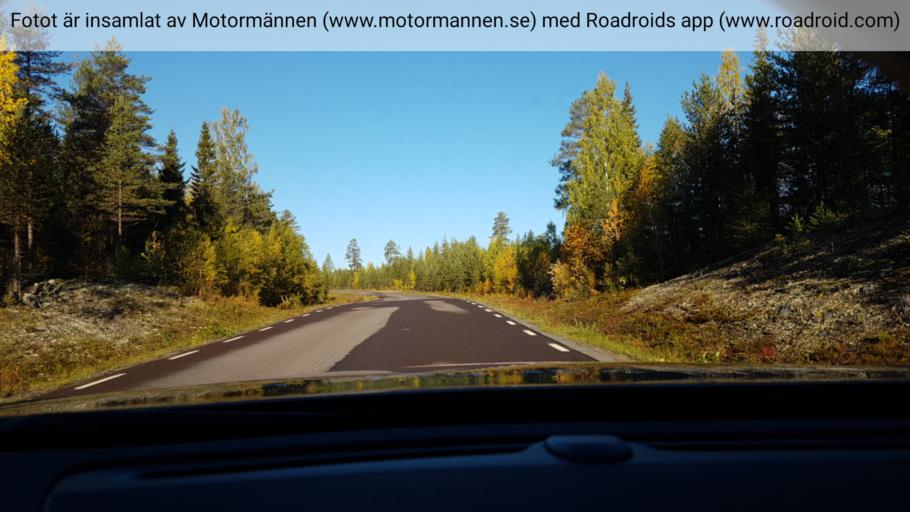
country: SE
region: Norrbotten
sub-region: Bodens Kommun
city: Boden
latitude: 66.0053
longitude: 21.5746
